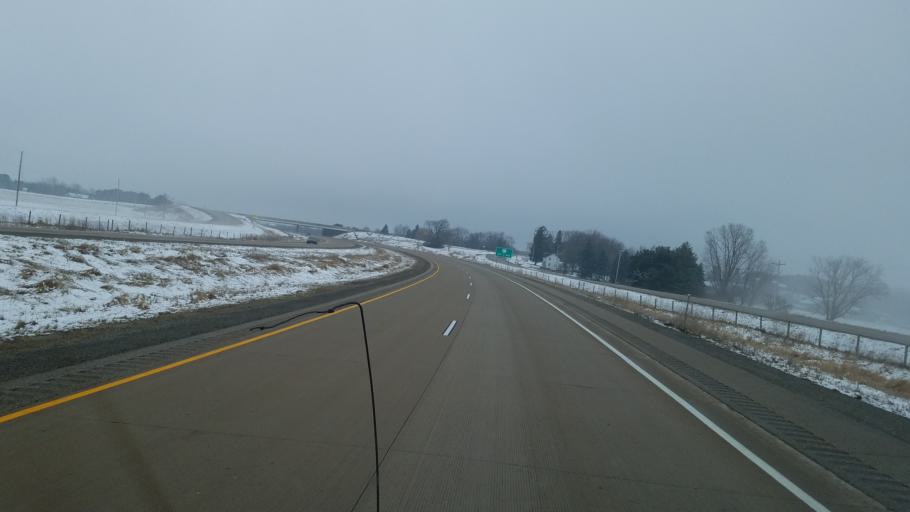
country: US
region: Wisconsin
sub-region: Winnebago County
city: Winneconne
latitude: 44.1793
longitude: -88.6644
